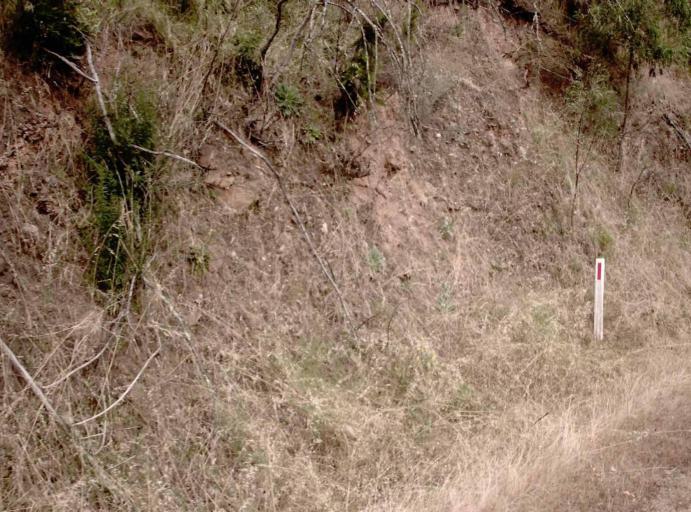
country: AU
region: Victoria
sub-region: Wellington
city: Heyfield
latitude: -37.7804
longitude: 146.6665
